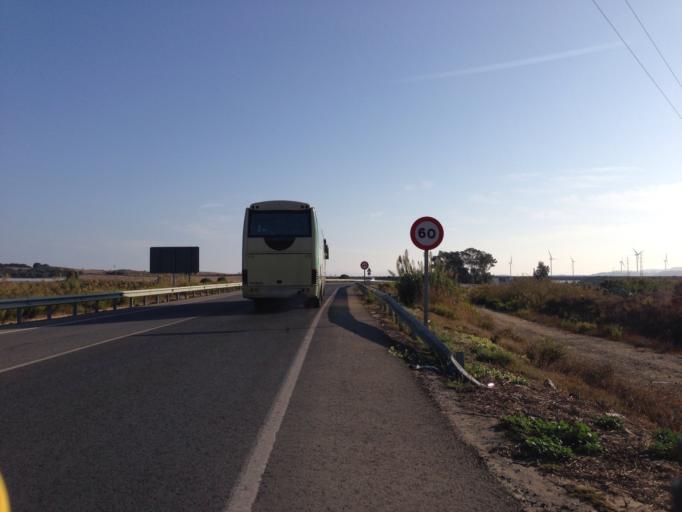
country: ES
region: Andalusia
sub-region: Provincia de Cadiz
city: Conil de la Frontera
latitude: 36.2904
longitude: -6.0629
